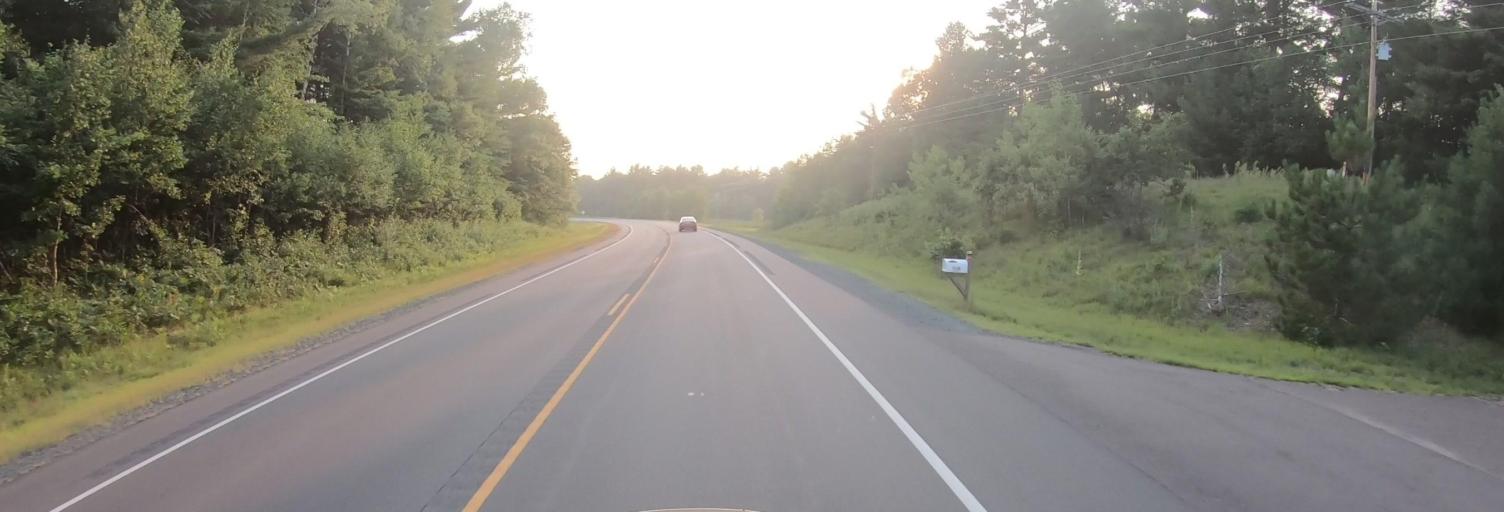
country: US
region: Wisconsin
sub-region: Burnett County
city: Siren
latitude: 45.8272
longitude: -92.2995
